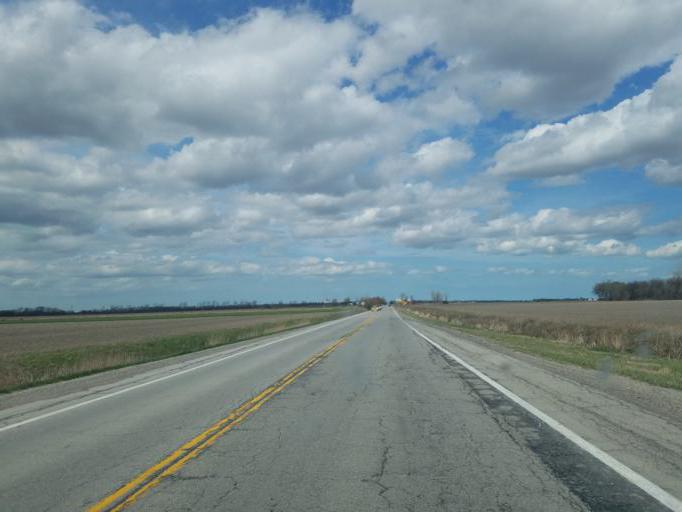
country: US
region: Ohio
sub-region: Huron County
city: Bellevue
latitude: 41.2993
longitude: -82.7788
